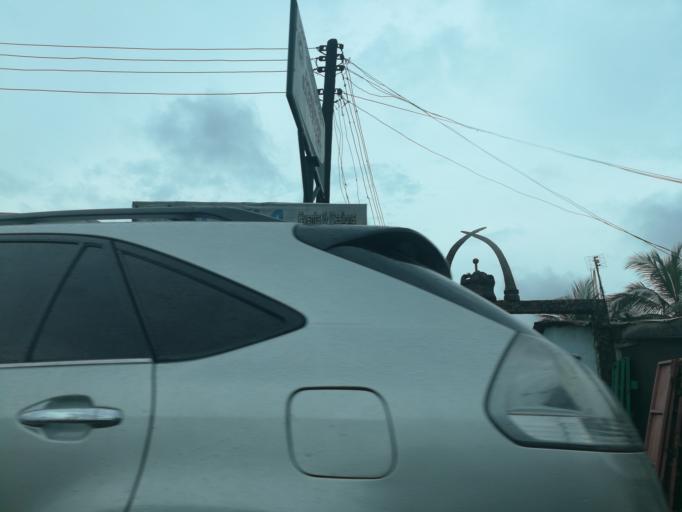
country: NG
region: Rivers
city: Port Harcourt
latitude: 4.8534
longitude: 7.0330
